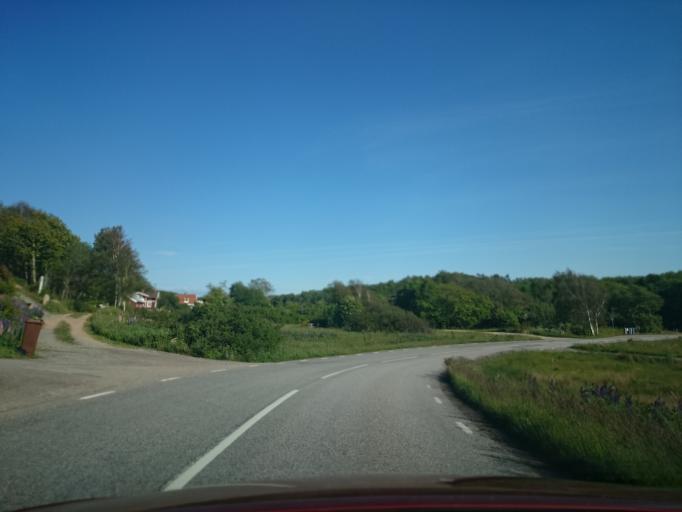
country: SE
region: Vaestra Goetaland
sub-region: Lysekils Kommun
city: Lysekil
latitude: 58.2441
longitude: 11.4686
